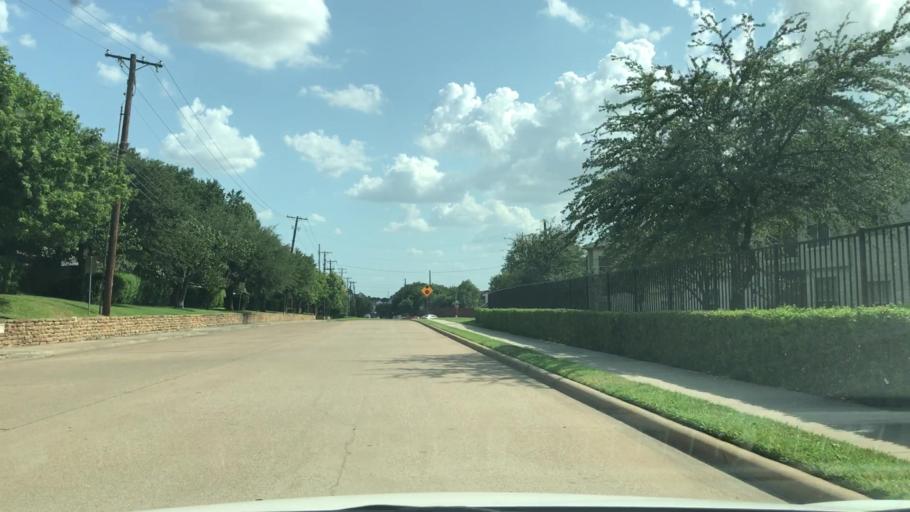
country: US
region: Texas
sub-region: Dallas County
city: Addison
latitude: 32.9721
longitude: -96.8515
